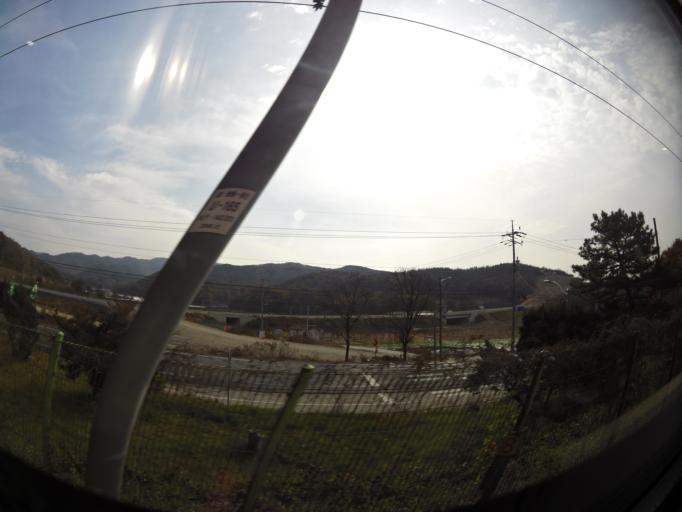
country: KR
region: Chungcheongbuk-do
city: Yong-dong
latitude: 36.1886
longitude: 127.8535
